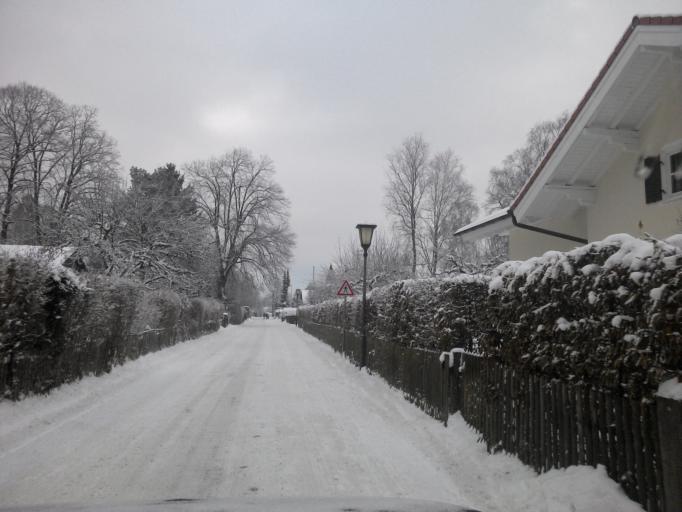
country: DE
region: Bavaria
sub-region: Upper Bavaria
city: Seeshaupt
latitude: 47.8233
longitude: 11.3024
